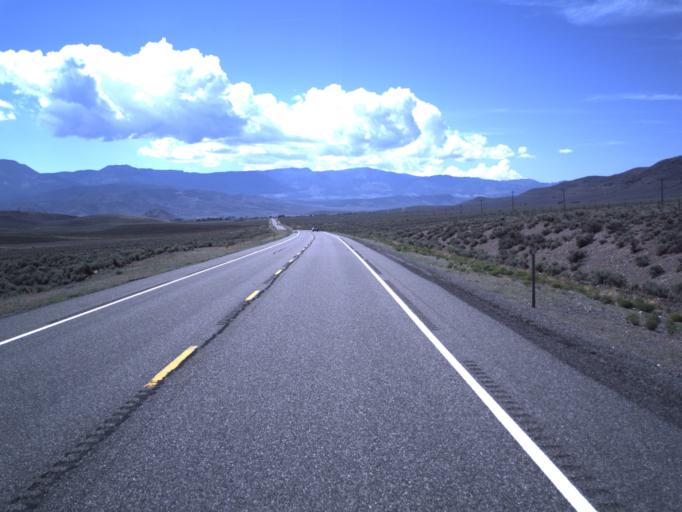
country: US
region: Utah
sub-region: Piute County
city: Junction
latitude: 38.2872
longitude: -112.2252
